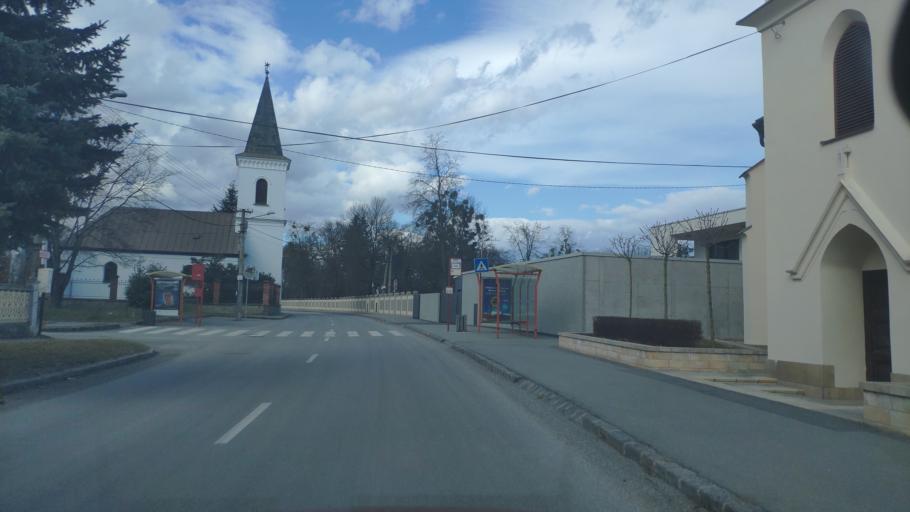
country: SK
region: Kosicky
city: Kosice
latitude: 48.6761
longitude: 21.2658
